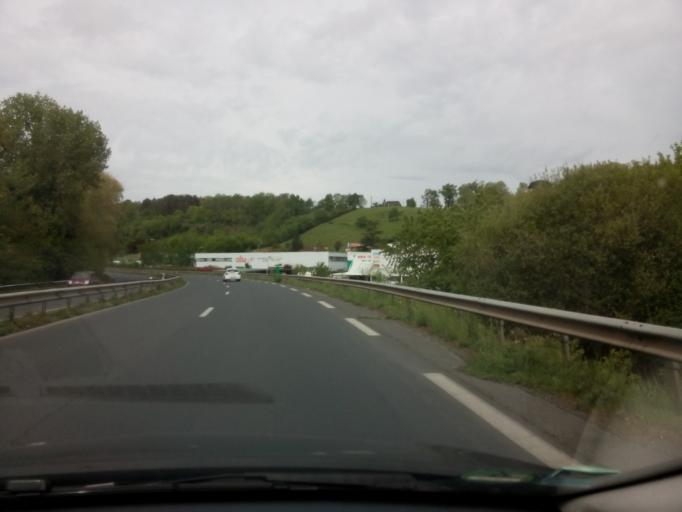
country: FR
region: Limousin
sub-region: Departement de la Correze
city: Ussac
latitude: 45.1632
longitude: 1.4949
